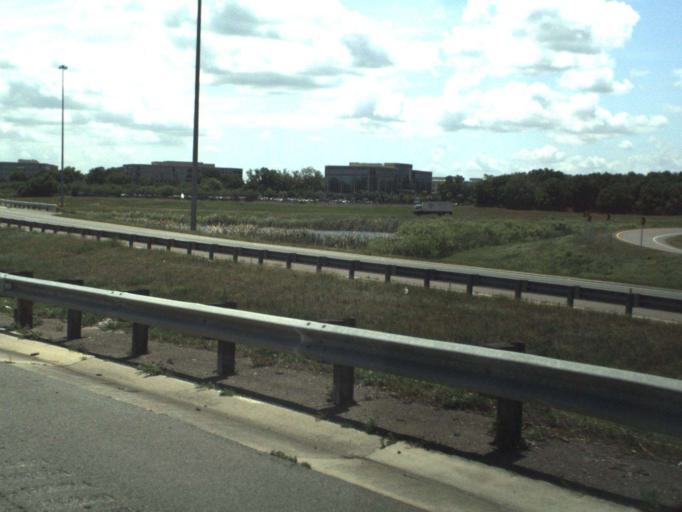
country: US
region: Florida
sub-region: Seminole County
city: Heathrow
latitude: 28.7937
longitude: -81.3470
